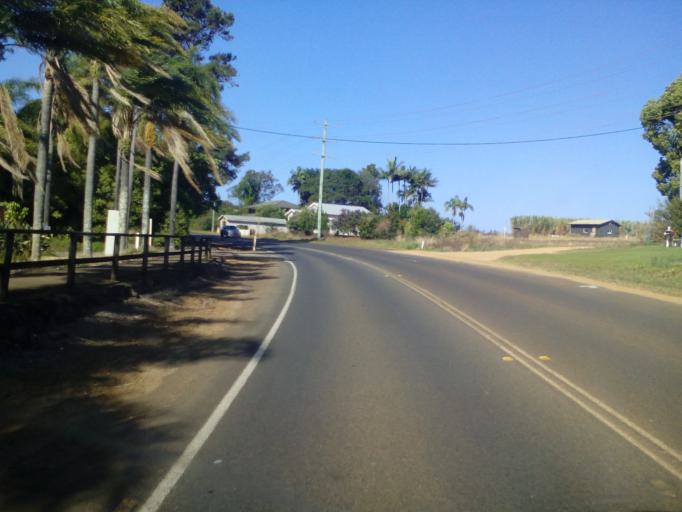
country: AU
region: New South Wales
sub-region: Tweed
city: Kingscliff
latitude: -28.2670
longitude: 153.5638
